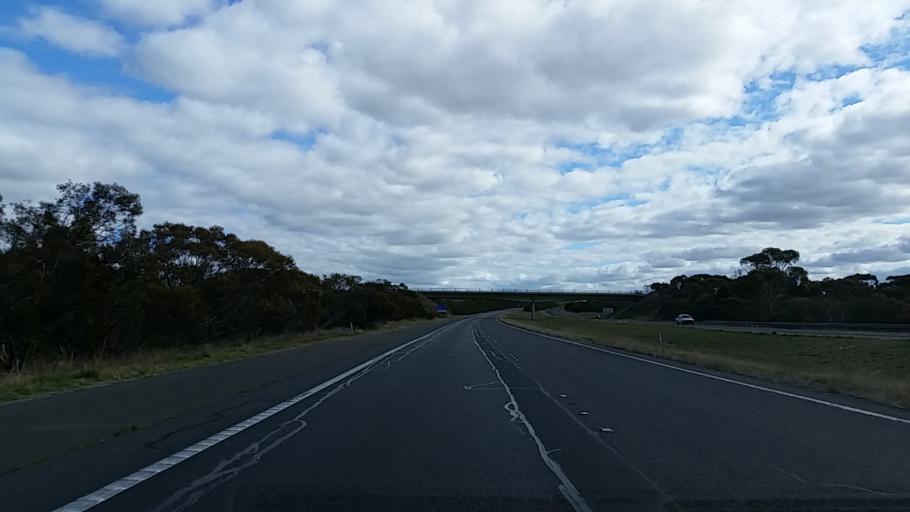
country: AU
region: South Australia
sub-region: Murray Bridge
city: Murray Bridge
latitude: -35.1525
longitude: 139.1957
